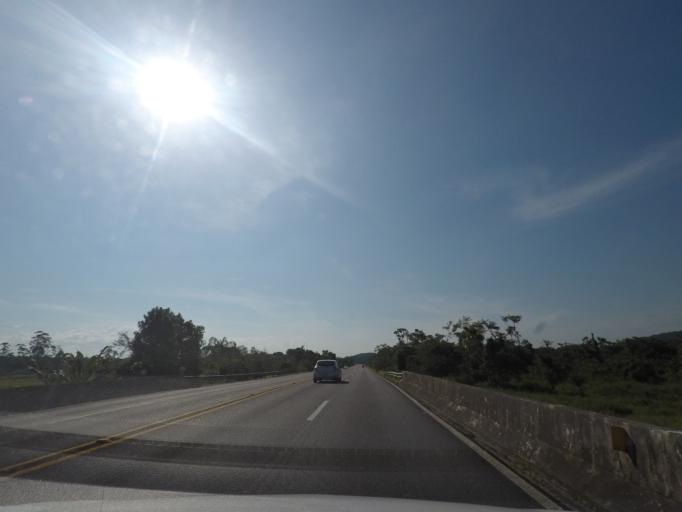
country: BR
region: Parana
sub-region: Paranagua
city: Paranagua
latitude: -25.5812
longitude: -48.6123
